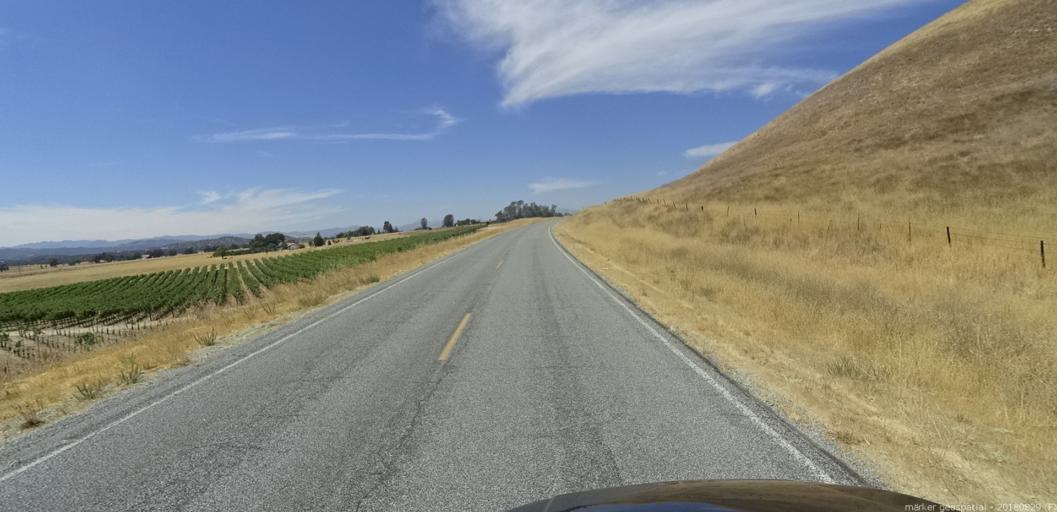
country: US
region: California
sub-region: San Luis Obispo County
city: Lake Nacimiento
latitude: 35.9108
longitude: -121.0191
